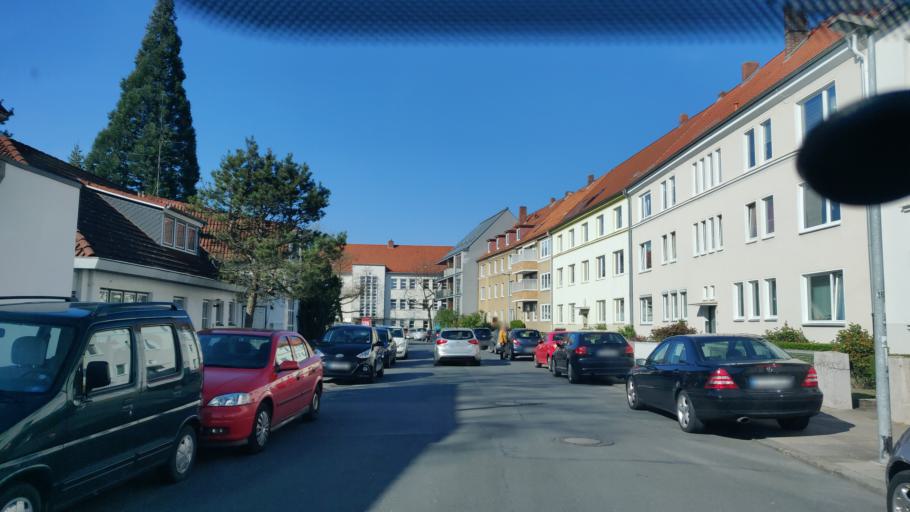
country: DE
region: Lower Saxony
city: Laatzen
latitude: 52.3592
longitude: 9.8264
